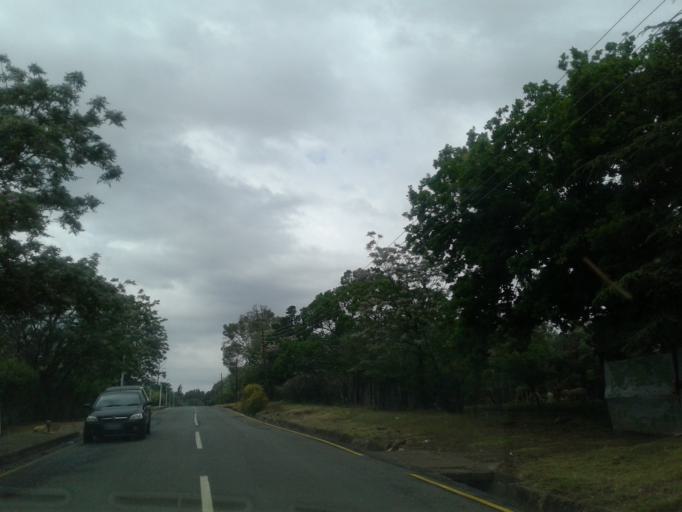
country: LS
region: Maseru
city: Maseru
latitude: -29.3040
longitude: 27.4692
